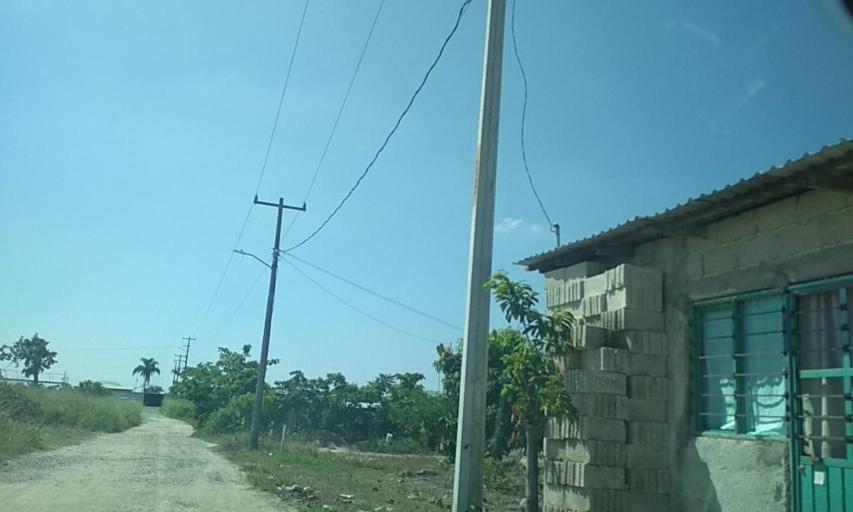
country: MX
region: Veracruz
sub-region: Martinez de la Torre
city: La Union Paso Largo
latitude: 20.1517
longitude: -96.9997
